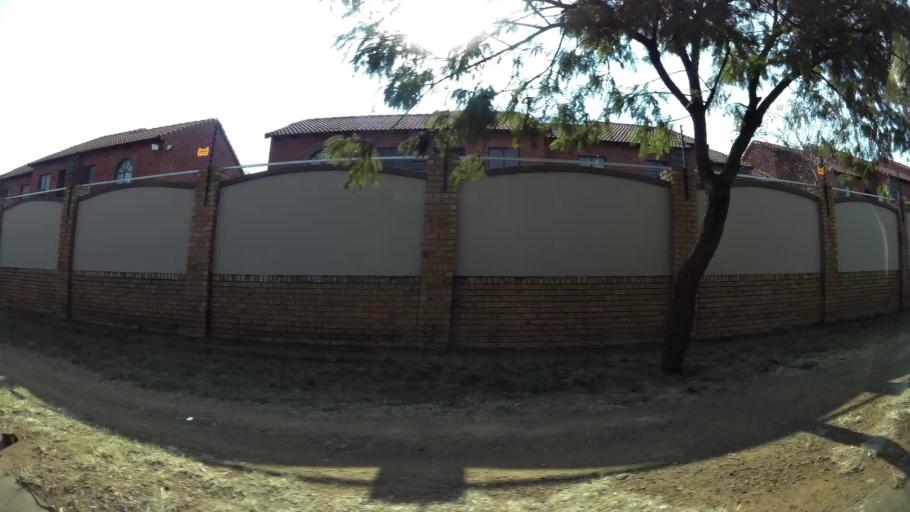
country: ZA
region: Gauteng
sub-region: City of Tshwane Metropolitan Municipality
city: Pretoria
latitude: -25.7637
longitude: 28.3447
